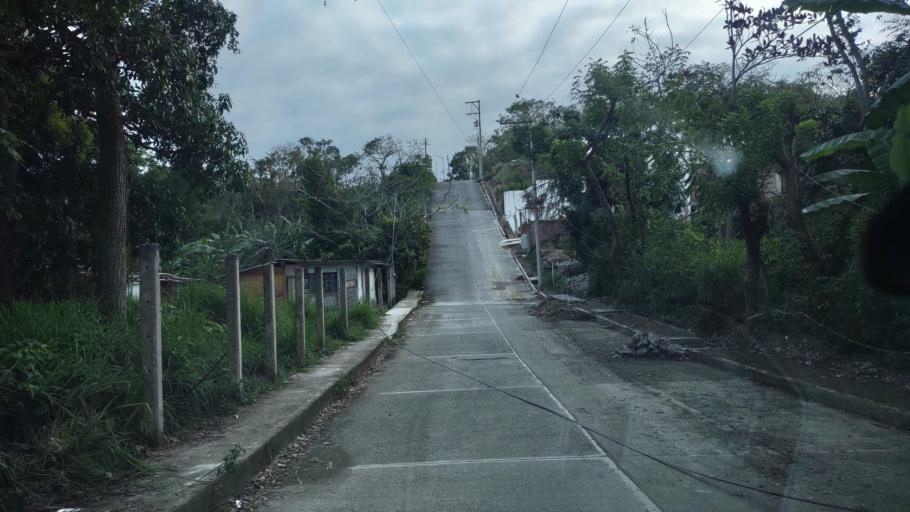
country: MX
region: Veracruz
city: Papantla de Olarte
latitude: 20.4544
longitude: -97.3060
